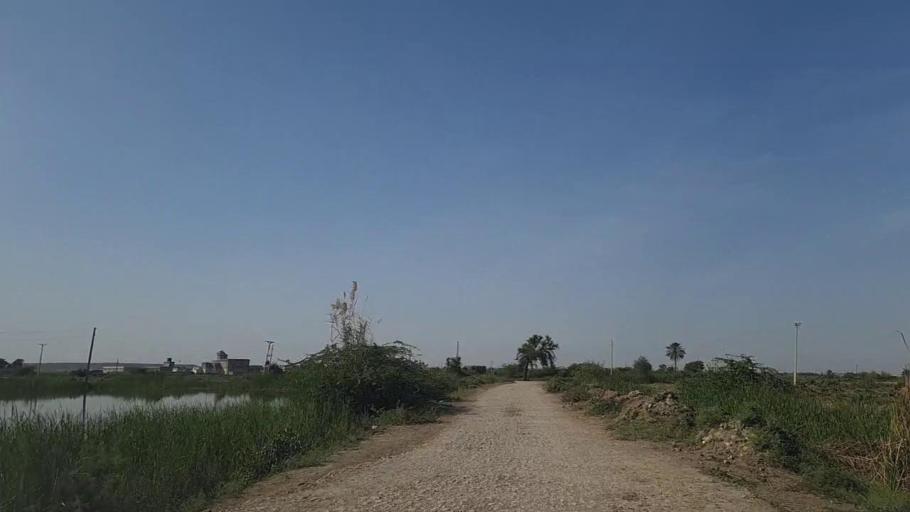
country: PK
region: Sindh
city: Thatta
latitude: 24.5917
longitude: 67.8885
